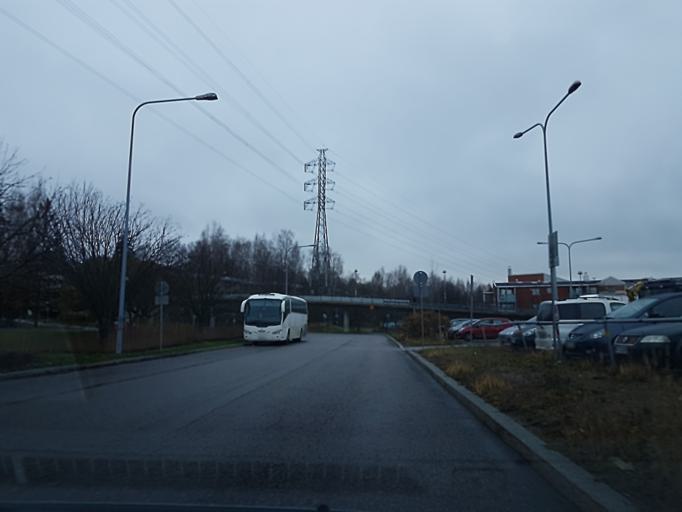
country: FI
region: Uusimaa
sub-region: Helsinki
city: Vantaa
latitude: 60.2384
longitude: 25.1075
